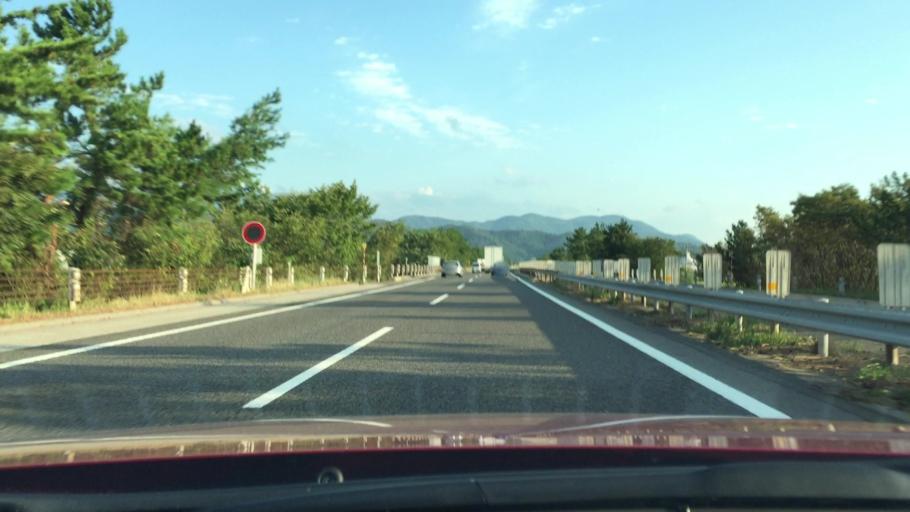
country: JP
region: Shiga Prefecture
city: Nagahama
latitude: 35.3770
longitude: 136.3023
